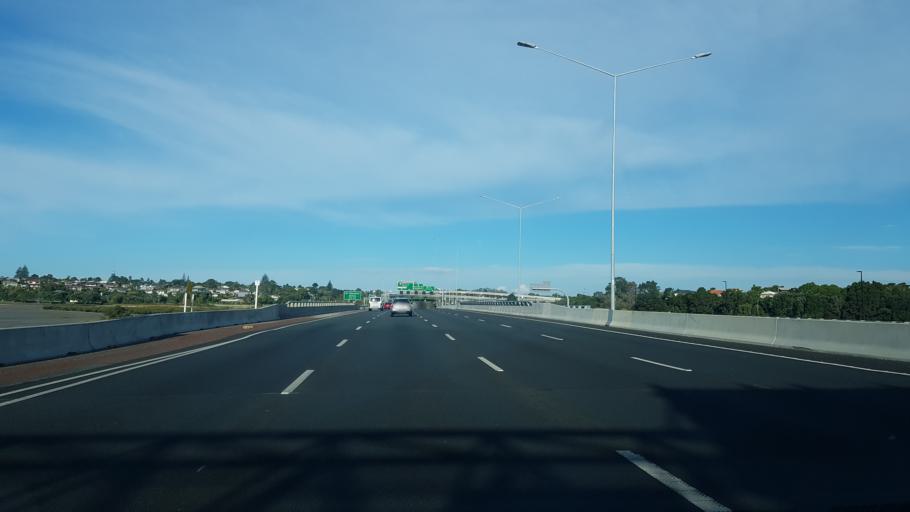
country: NZ
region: Auckland
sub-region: Auckland
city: Rosebank
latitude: -36.8716
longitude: 174.6916
